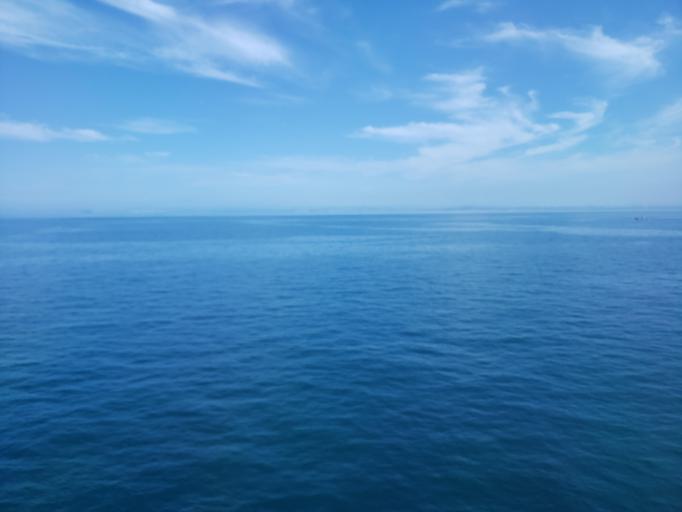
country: JP
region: Hyogo
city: Akashi
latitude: 34.5646
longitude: 134.7897
